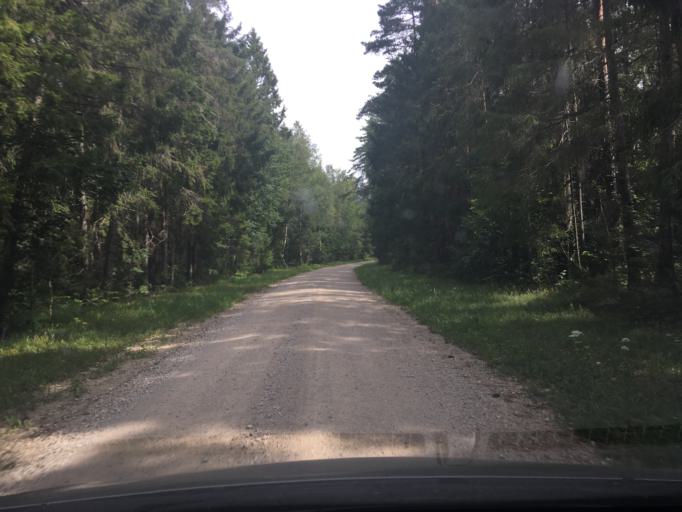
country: EE
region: Raplamaa
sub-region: Maerjamaa vald
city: Marjamaa
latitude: 58.9500
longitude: 24.5698
